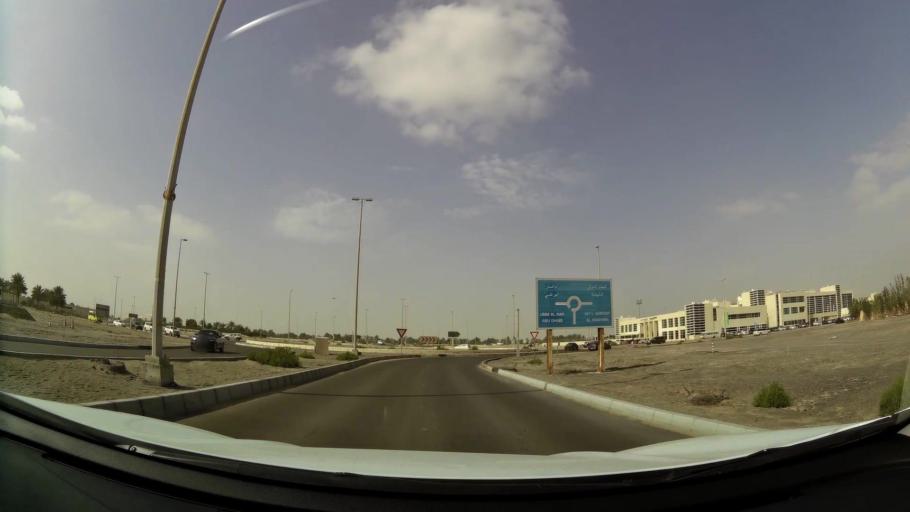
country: AE
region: Abu Dhabi
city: Abu Dhabi
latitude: 24.4239
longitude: 54.5458
